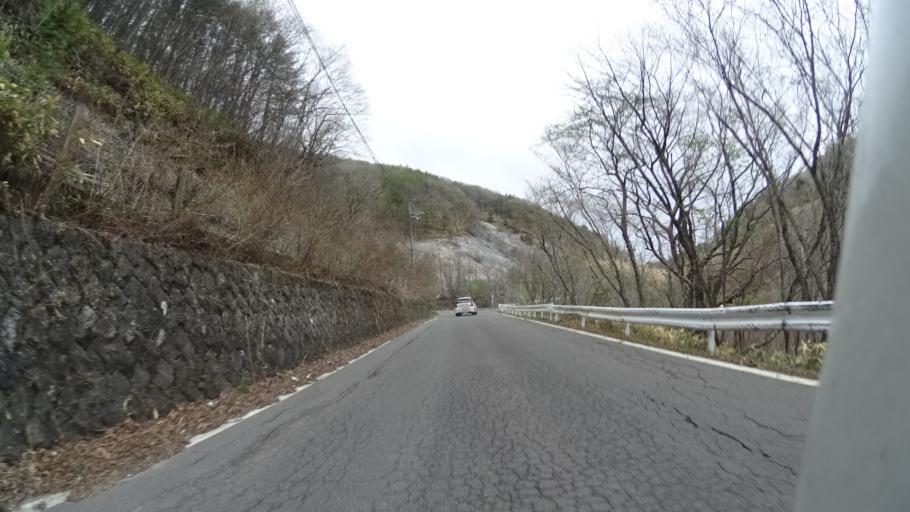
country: JP
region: Nagano
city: Suwa
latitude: 36.1417
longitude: 138.1435
